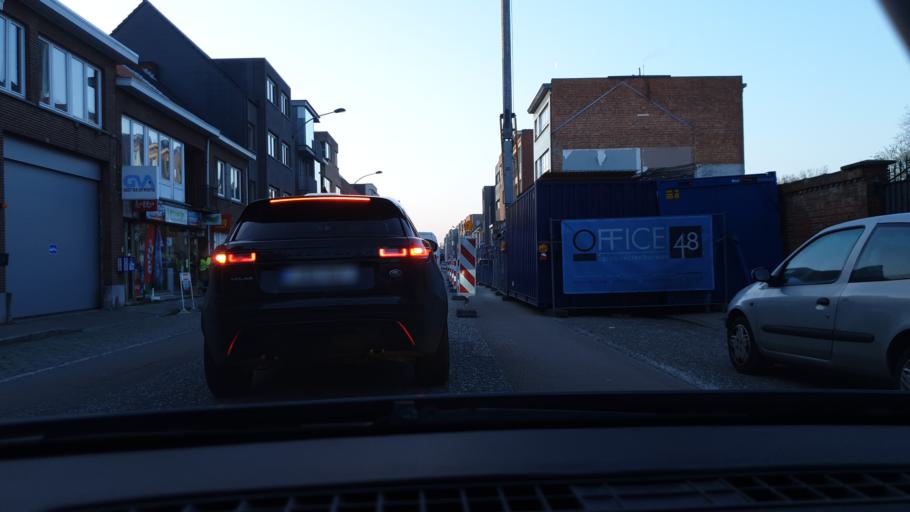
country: BE
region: Flanders
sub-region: Provincie Antwerpen
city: Geel
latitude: 51.1602
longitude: 4.9916
